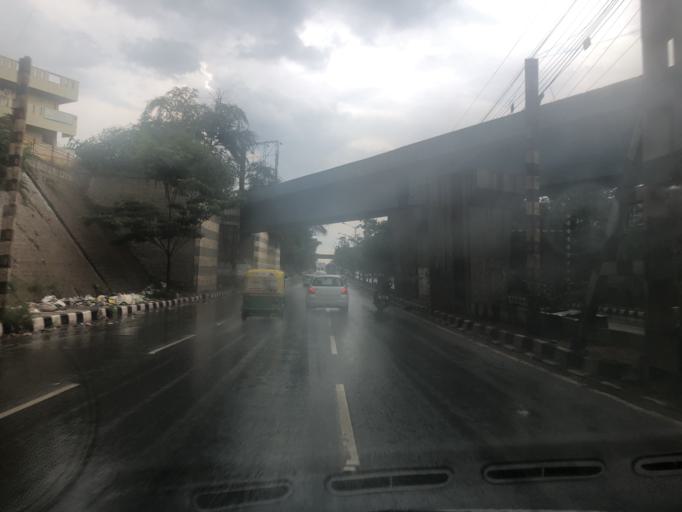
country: IN
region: Karnataka
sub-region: Bangalore Urban
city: Bangalore
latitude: 12.9724
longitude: 77.6989
